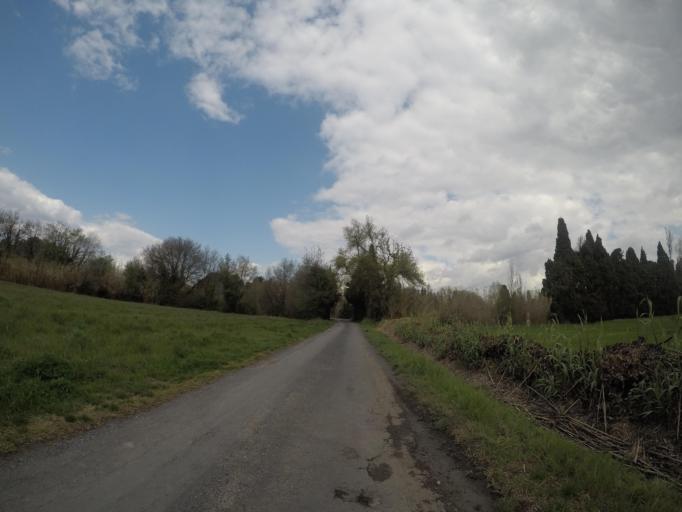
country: FR
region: Languedoc-Roussillon
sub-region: Departement des Pyrenees-Orientales
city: Pezilla-la-Riviere
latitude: 42.6909
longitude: 2.7761
